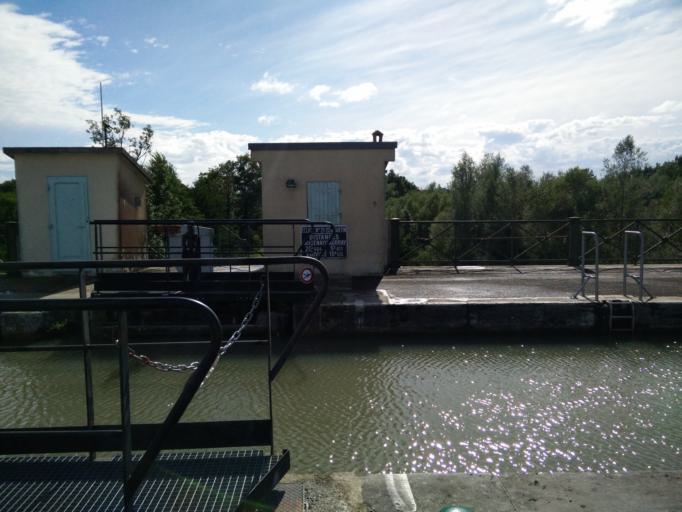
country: FR
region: Centre
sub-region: Departement du Cher
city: Cuffy
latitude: 46.9465
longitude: 3.0703
